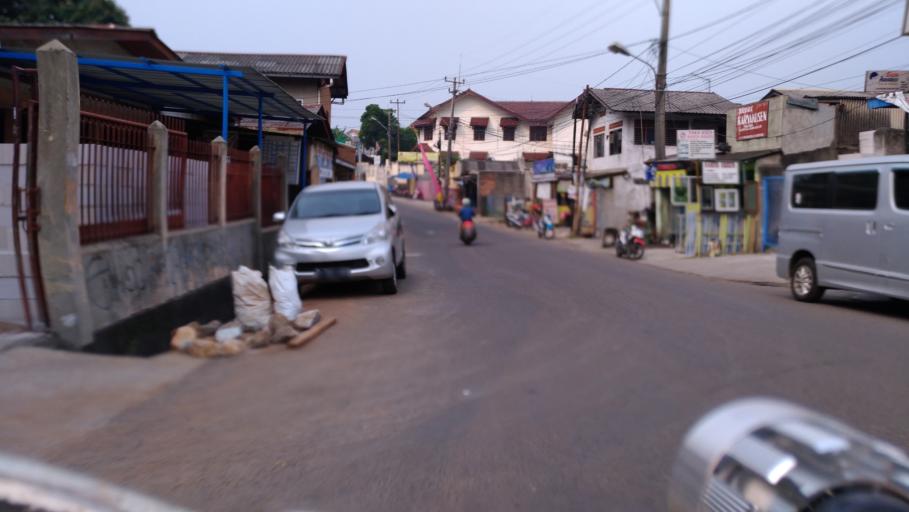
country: ID
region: West Java
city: Depok
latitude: -6.3658
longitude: 106.8611
